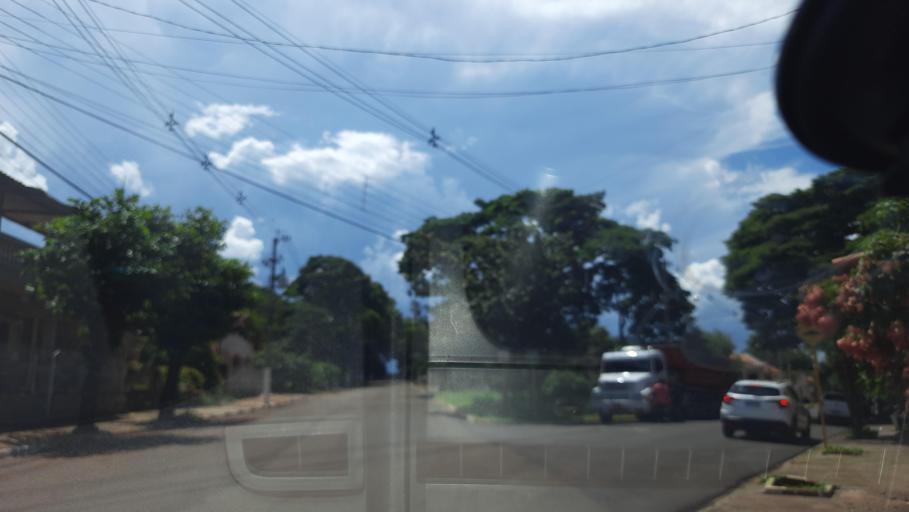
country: BR
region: Sao Paulo
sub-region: Casa Branca
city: Casa Branca
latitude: -21.7819
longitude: -47.0736
